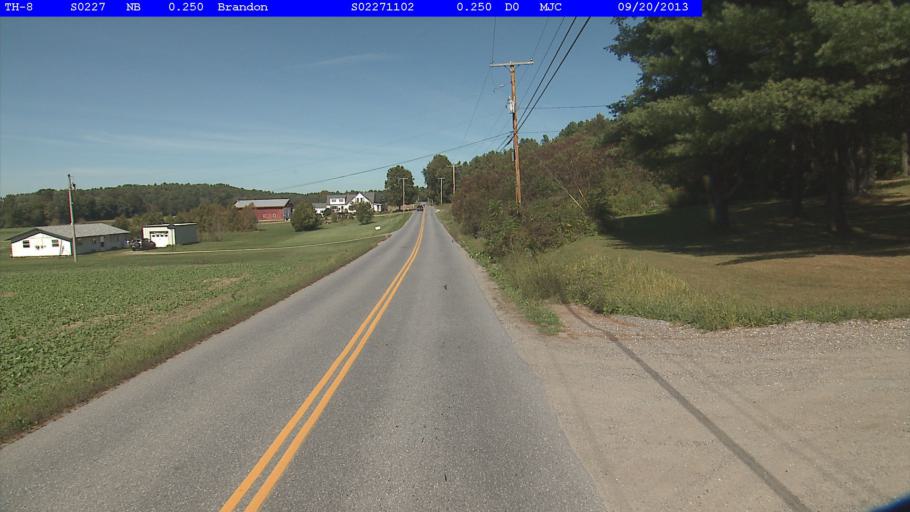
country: US
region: Vermont
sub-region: Rutland County
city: Brandon
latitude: 43.7780
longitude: -73.0521
